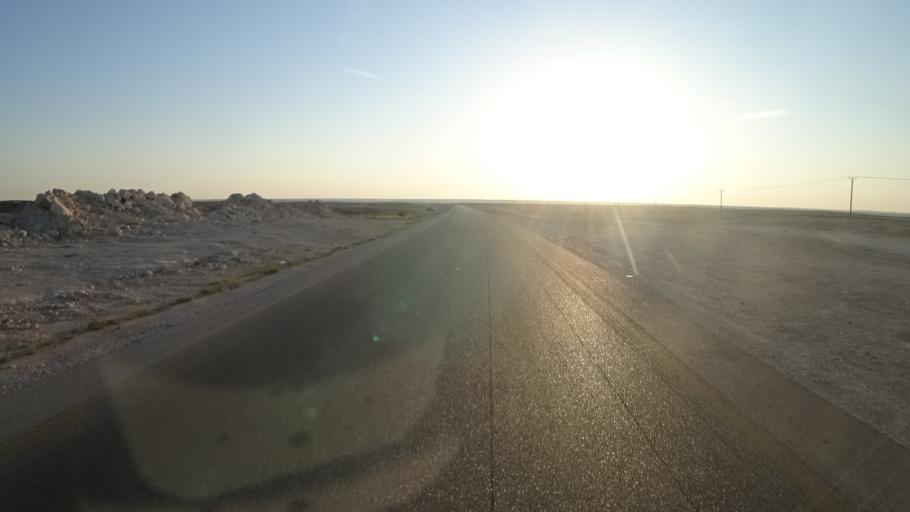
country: OM
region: Zufar
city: Salalah
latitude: 17.5376
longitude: 53.4108
